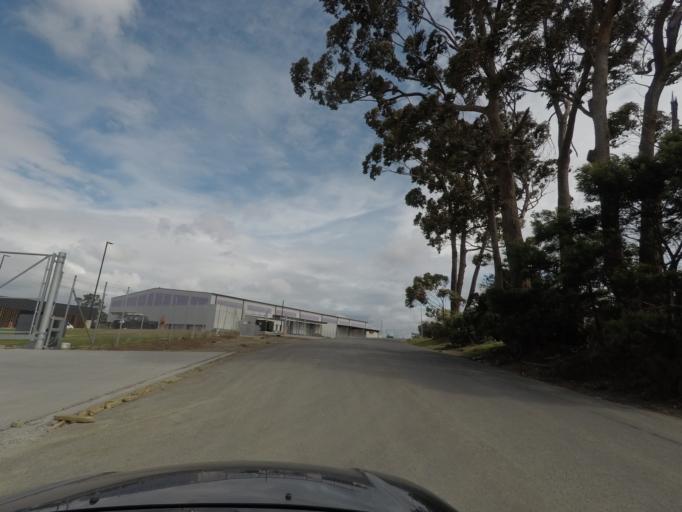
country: NZ
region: Auckland
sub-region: Auckland
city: Rosebank
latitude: -36.8442
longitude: 174.6321
